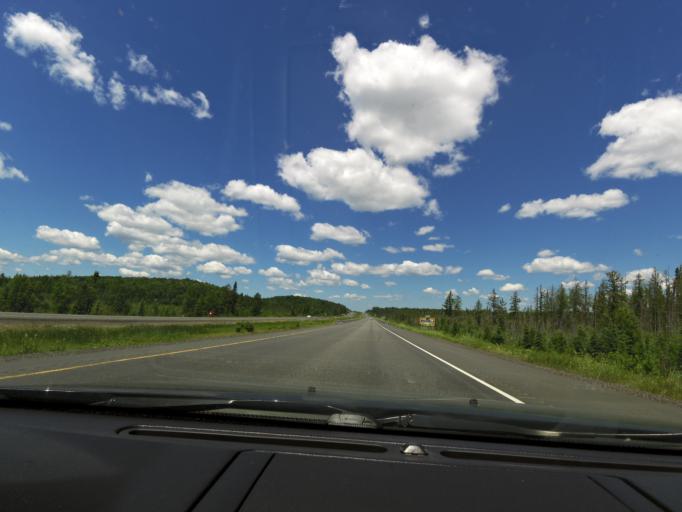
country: CA
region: Ontario
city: Huntsville
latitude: 45.4743
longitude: -79.2704
